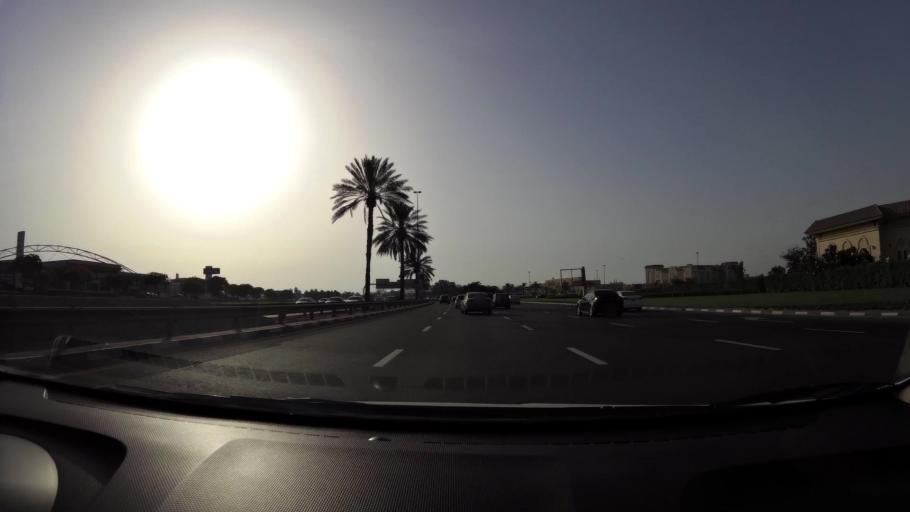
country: AE
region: Ash Shariqah
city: Sharjah
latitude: 25.2338
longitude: 55.3502
